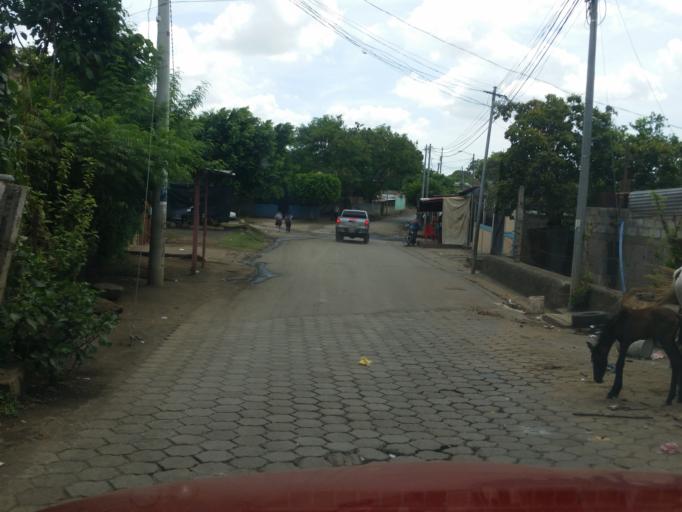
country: NI
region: Managua
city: Managua
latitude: 12.1054
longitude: -86.2296
